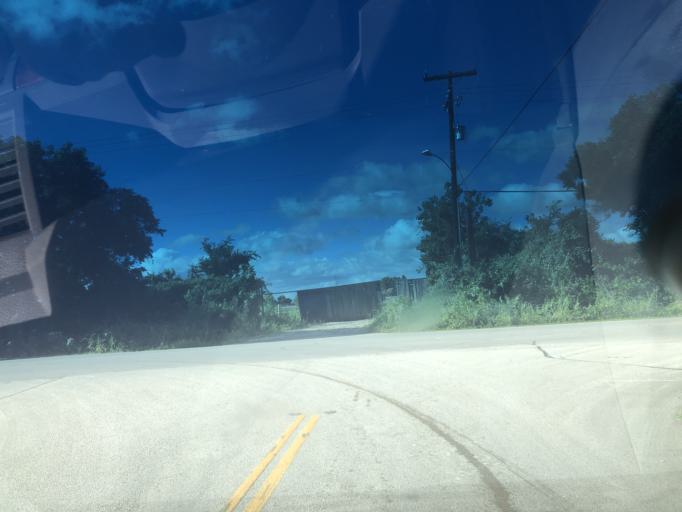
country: US
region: Texas
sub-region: Dallas County
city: Grand Prairie
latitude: 32.7927
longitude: -97.0203
